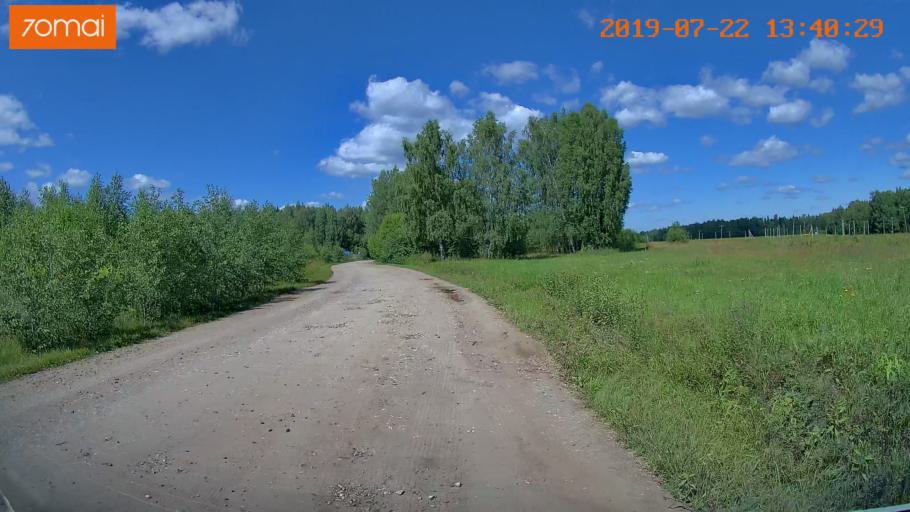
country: RU
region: Ivanovo
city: Novo-Talitsy
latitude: 57.0765
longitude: 40.8811
